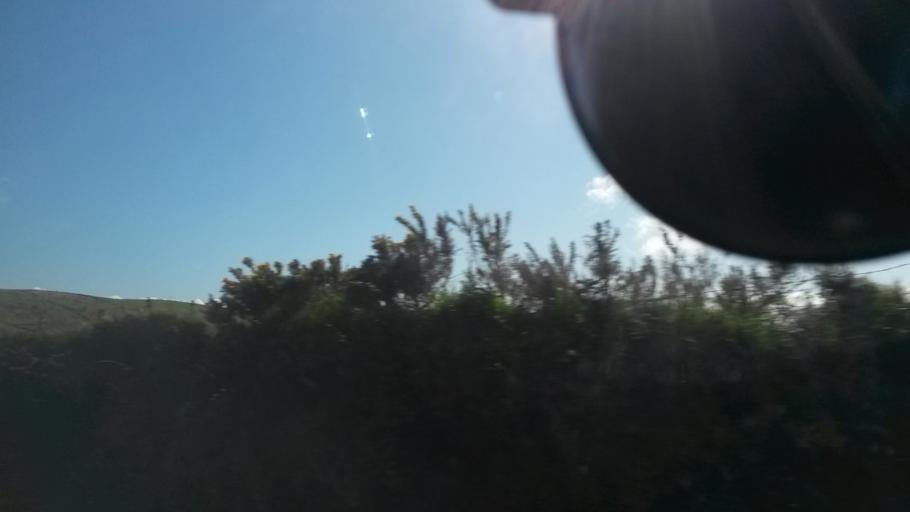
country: IE
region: Munster
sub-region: Ciarrai
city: Dingle
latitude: 52.1534
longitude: -10.2449
